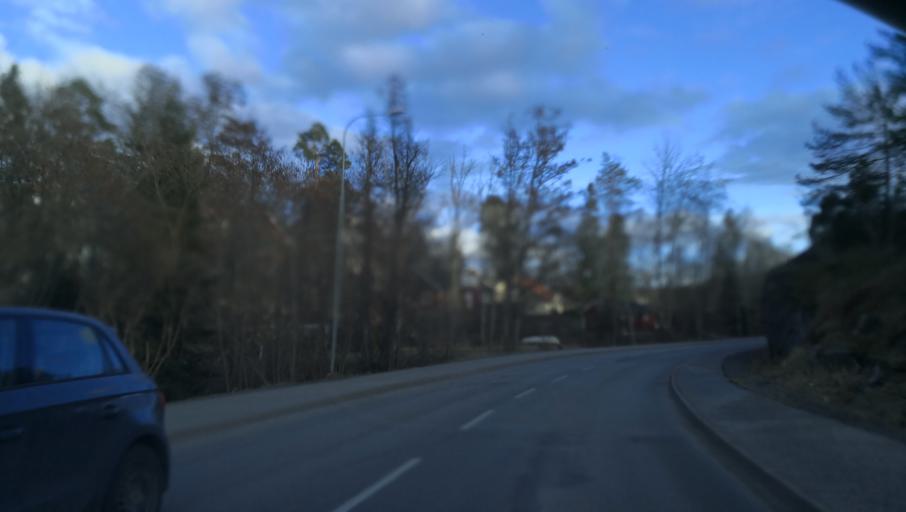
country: SE
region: Stockholm
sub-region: Varmdo Kommun
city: Gustavsberg
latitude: 59.3334
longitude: 18.3369
